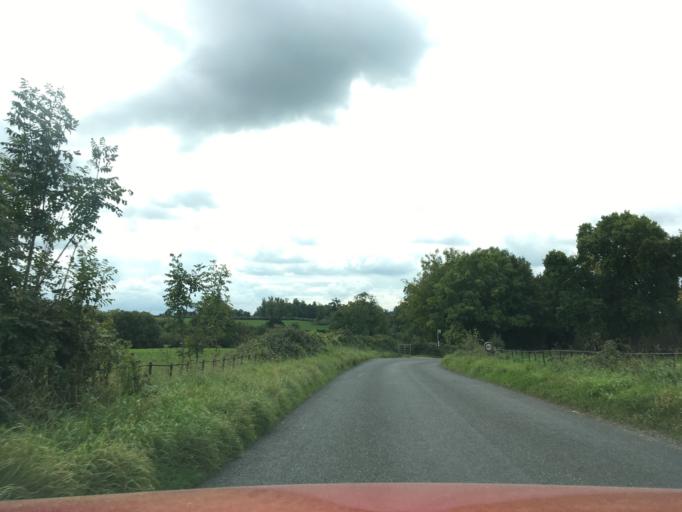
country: GB
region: England
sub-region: South Gloucestershire
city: Charfield
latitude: 51.6312
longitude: -2.4332
